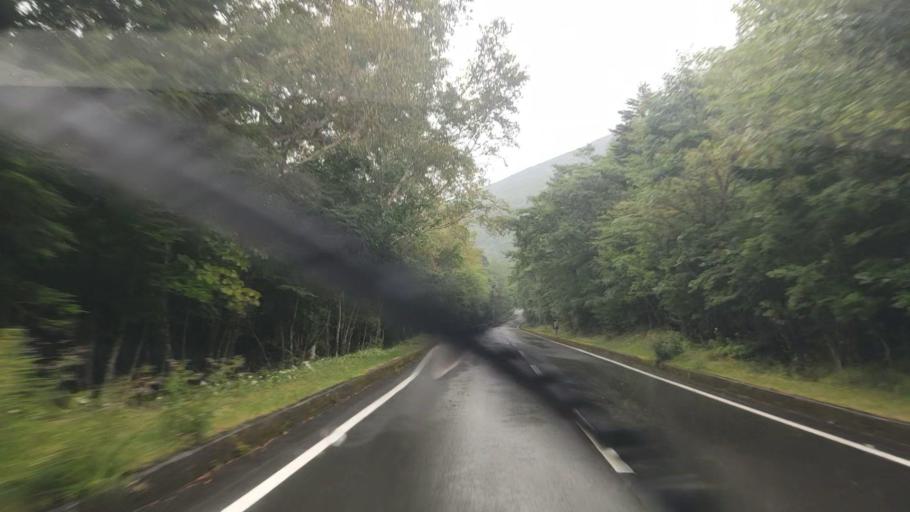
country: JP
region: Shizuoka
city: Fujinomiya
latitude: 35.3218
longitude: 138.7210
